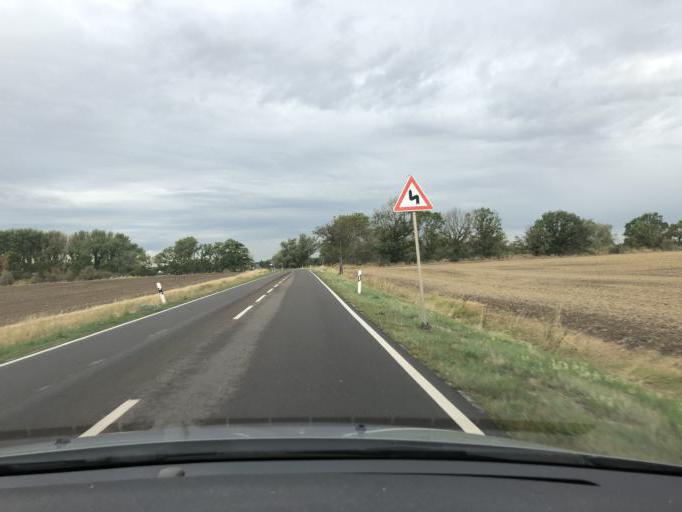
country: DE
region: Saxony-Anhalt
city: Calbe
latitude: 51.8876
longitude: 11.8077
